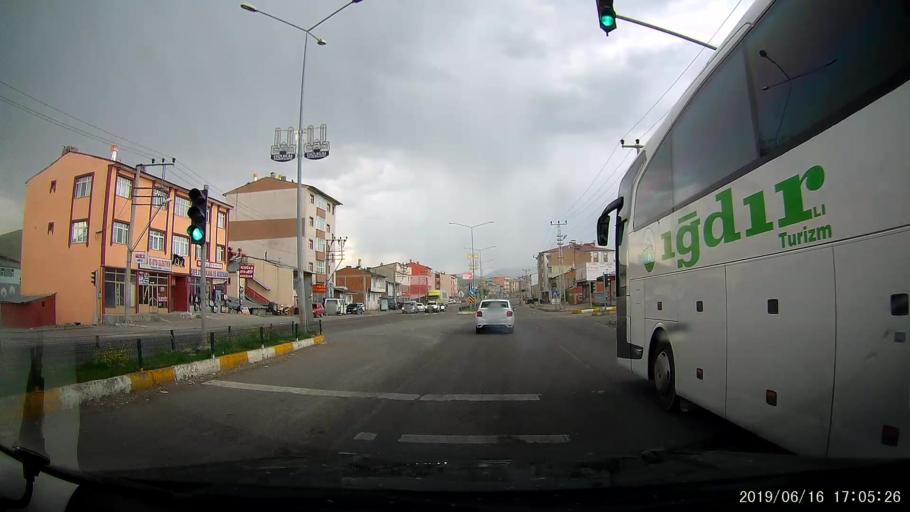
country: TR
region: Erzurum
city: Askale
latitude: 39.9220
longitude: 40.7008
